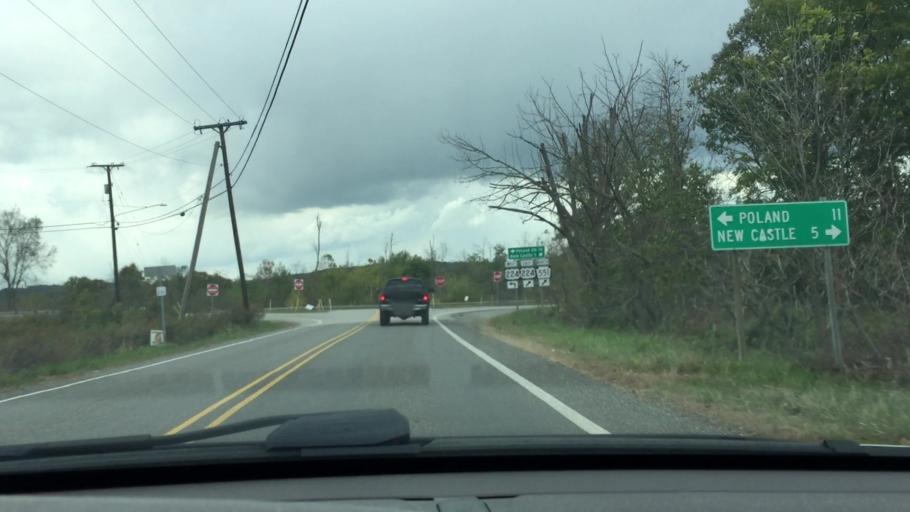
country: US
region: Pennsylvania
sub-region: Lawrence County
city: Oakwood
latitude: 41.0148
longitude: -80.4425
